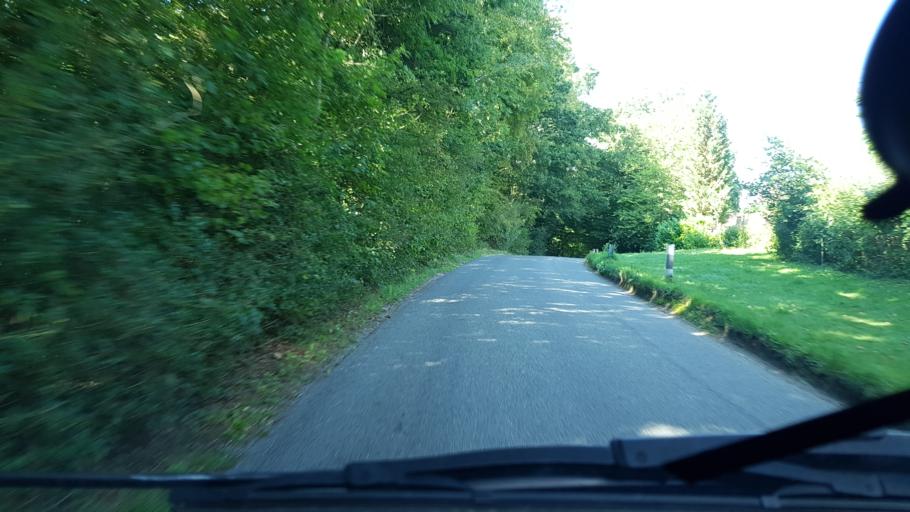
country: GB
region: England
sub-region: Surrey
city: Ockley
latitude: 51.1000
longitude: -0.3633
